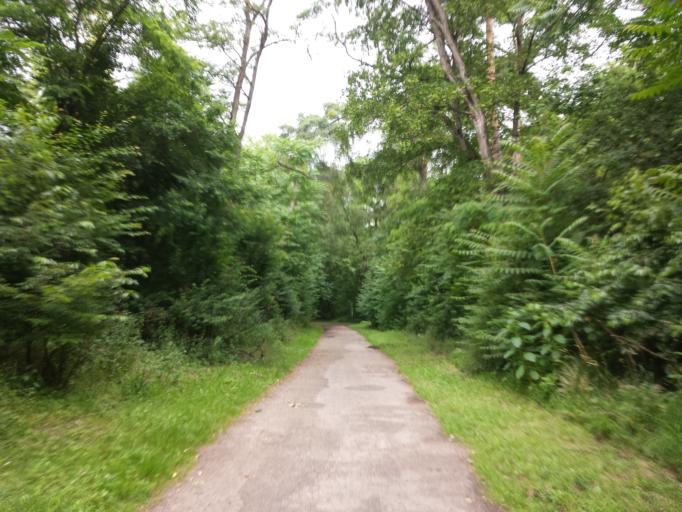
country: DE
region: Hesse
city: Viernheim
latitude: 49.5296
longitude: 8.5324
